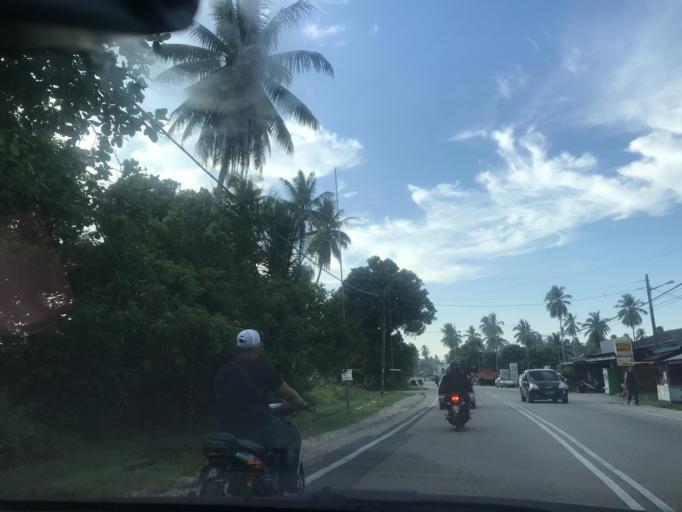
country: MY
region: Kelantan
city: Peringat
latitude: 6.1232
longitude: 102.3570
